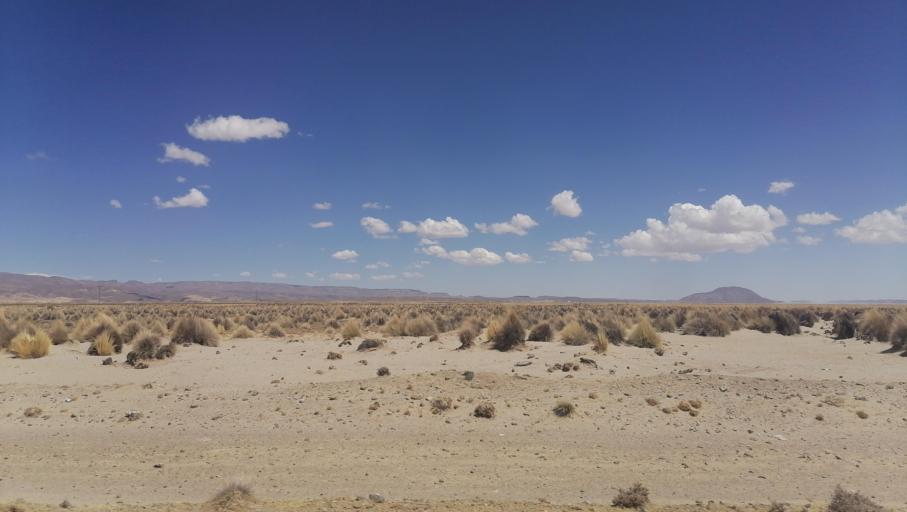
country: BO
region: Oruro
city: Challapata
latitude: -19.1717
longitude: -66.7970
